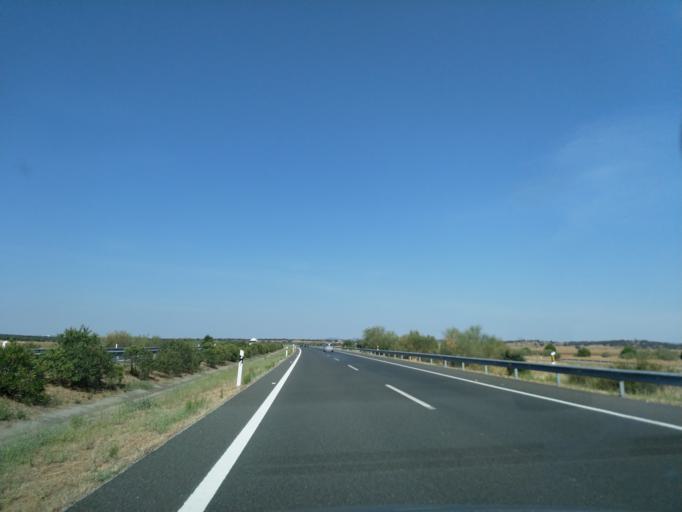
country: ES
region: Extremadura
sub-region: Provincia de Caceres
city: Casas de Don Antonio
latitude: 39.2508
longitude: -6.3079
